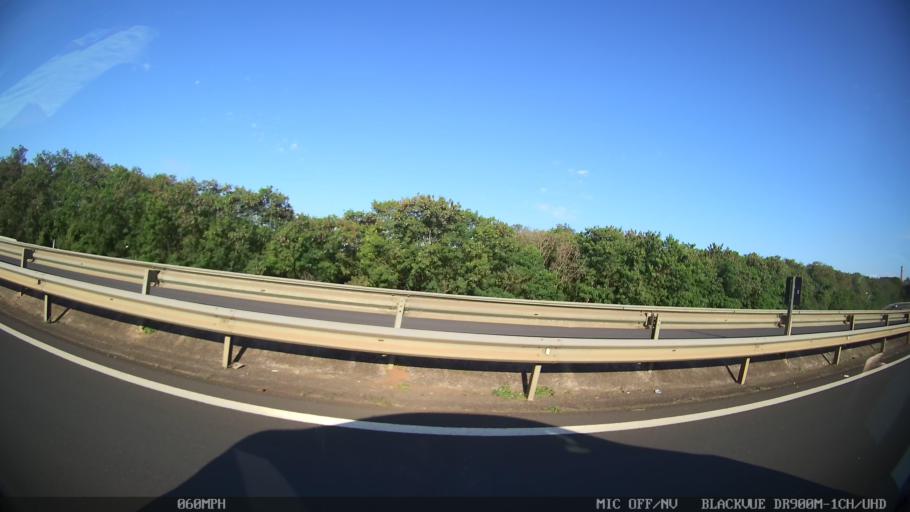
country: BR
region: Sao Paulo
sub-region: Piracicaba
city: Piracicaba
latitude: -22.6935
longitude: -47.6356
